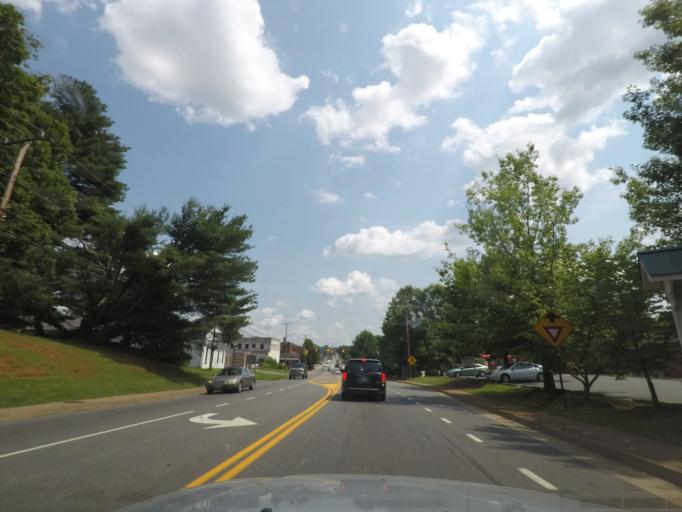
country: US
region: Virginia
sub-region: Orange County
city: Orange
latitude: 38.2537
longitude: -78.1150
